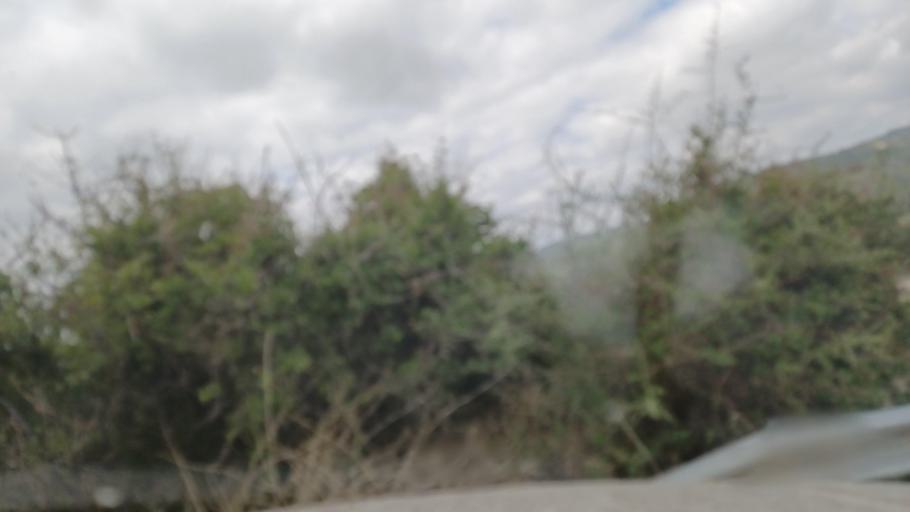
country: CY
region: Limassol
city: Pachna
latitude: 34.7792
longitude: 32.6839
